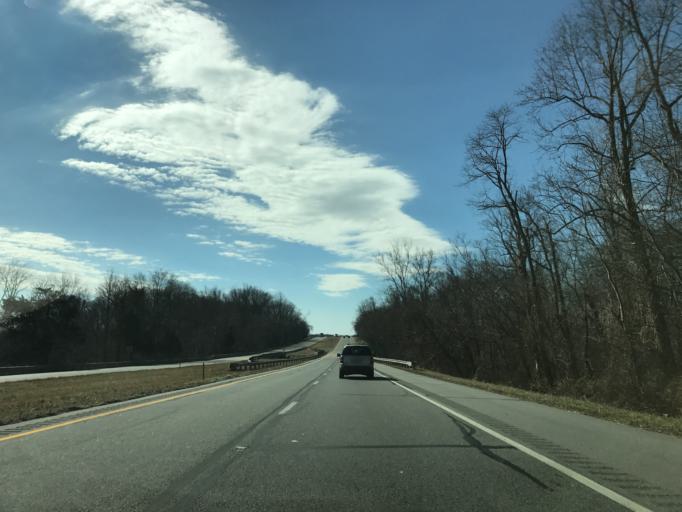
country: US
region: Delaware
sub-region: New Castle County
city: Middletown
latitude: 39.3788
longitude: -75.8065
